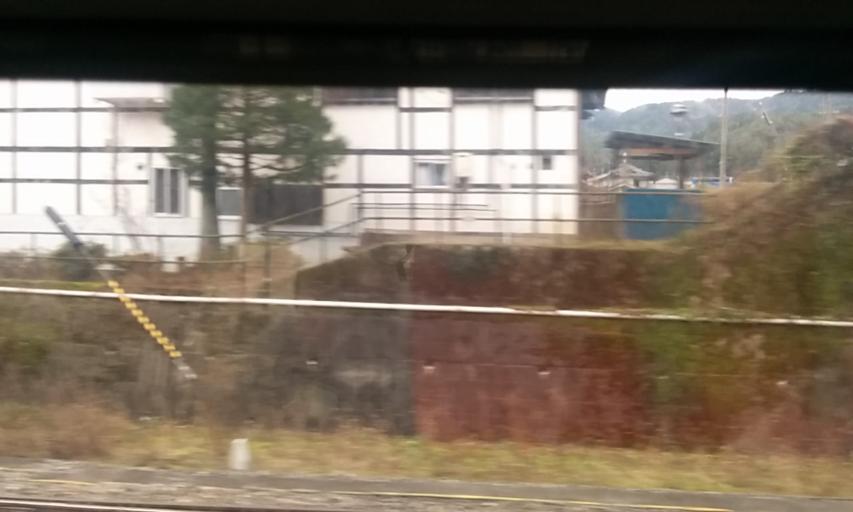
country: JP
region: Nagano
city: Ina
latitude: 35.8420
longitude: 137.6919
